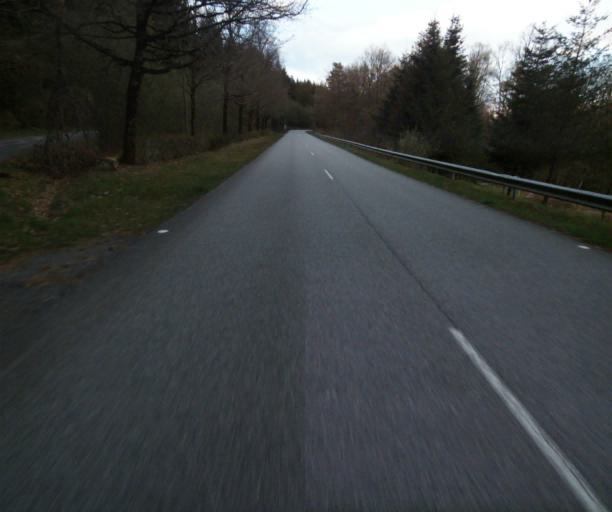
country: FR
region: Limousin
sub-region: Departement de la Correze
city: Correze
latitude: 45.2887
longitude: 1.8737
